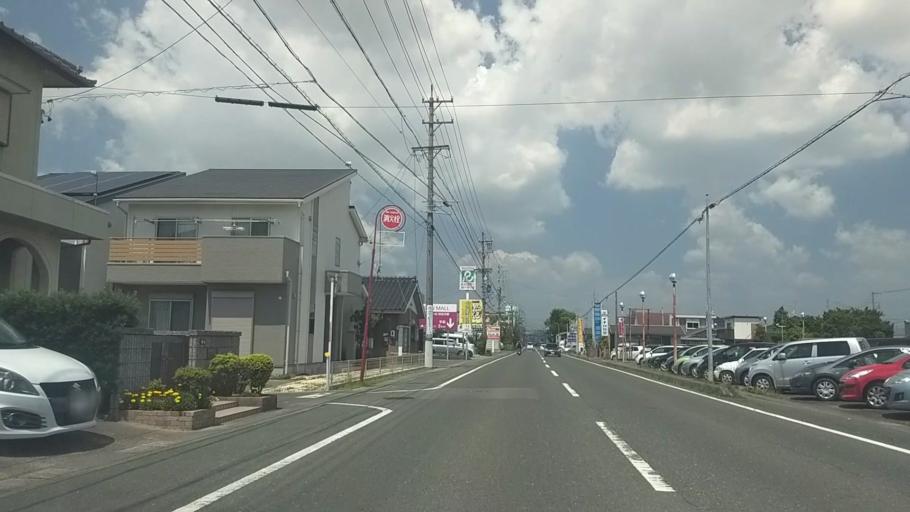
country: JP
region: Shizuoka
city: Hamamatsu
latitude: 34.7551
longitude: 137.7319
